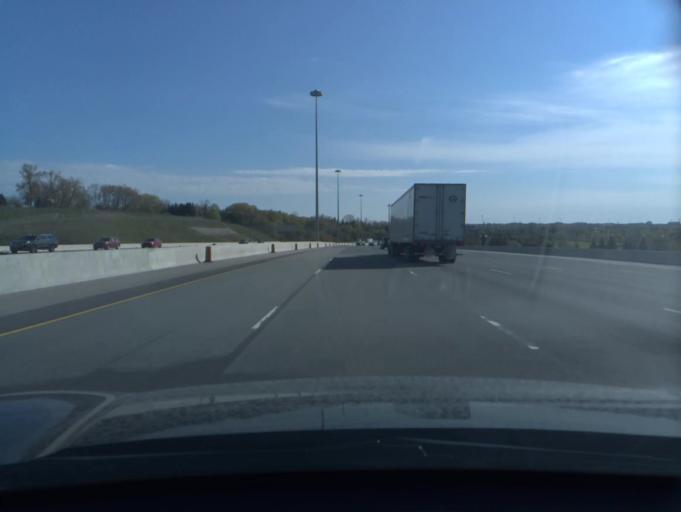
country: CA
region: Ontario
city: North Perth
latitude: 43.8190
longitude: -80.9998
